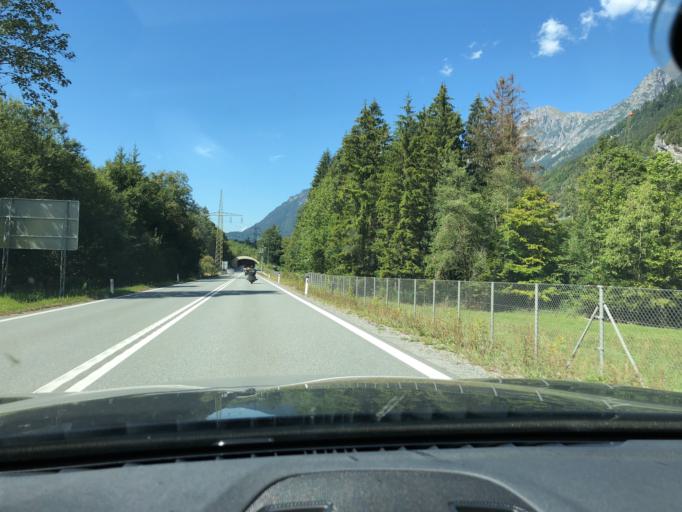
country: AT
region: Vorarlberg
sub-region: Politischer Bezirk Bludenz
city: Innerbraz
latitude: 47.1345
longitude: 9.9450
